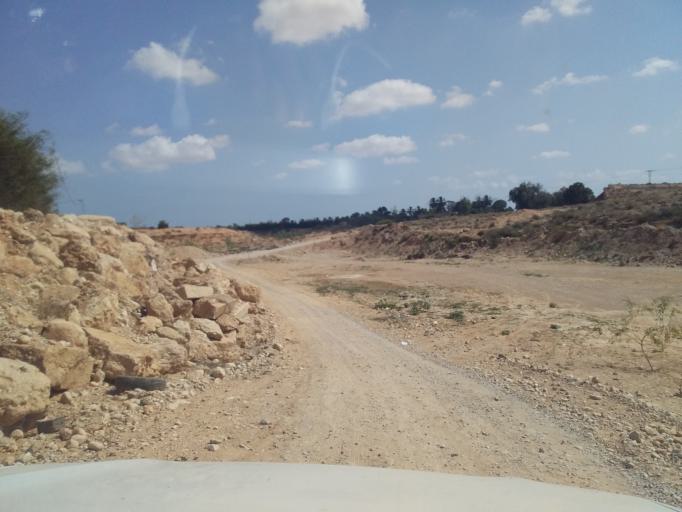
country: TN
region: Madanin
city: Medenine
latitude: 33.6013
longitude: 10.3179
